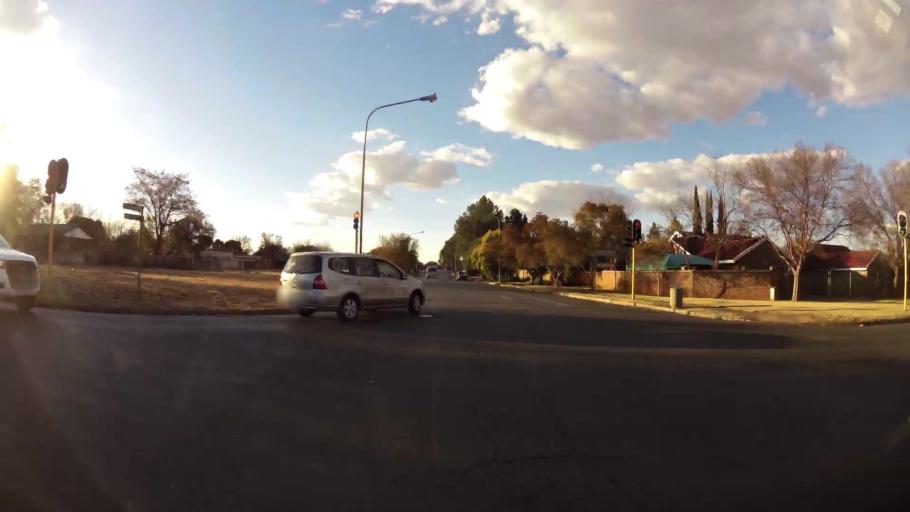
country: ZA
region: North-West
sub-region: Dr Kenneth Kaunda District Municipality
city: Potchefstroom
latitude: -26.7309
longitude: 27.0955
